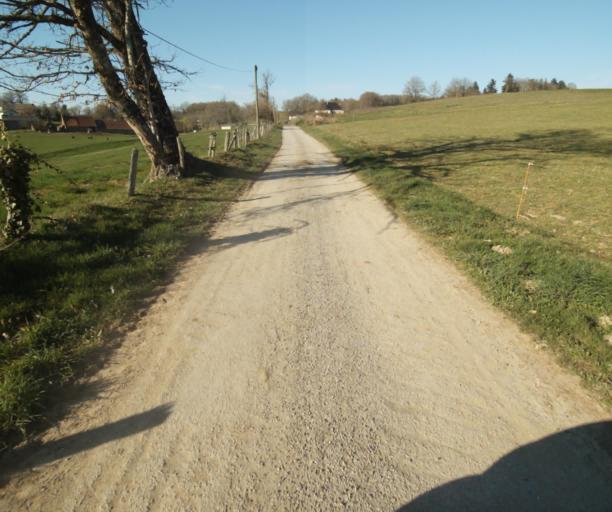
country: FR
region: Limousin
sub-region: Departement de la Correze
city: Chamboulive
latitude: 45.4950
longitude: 1.7285
